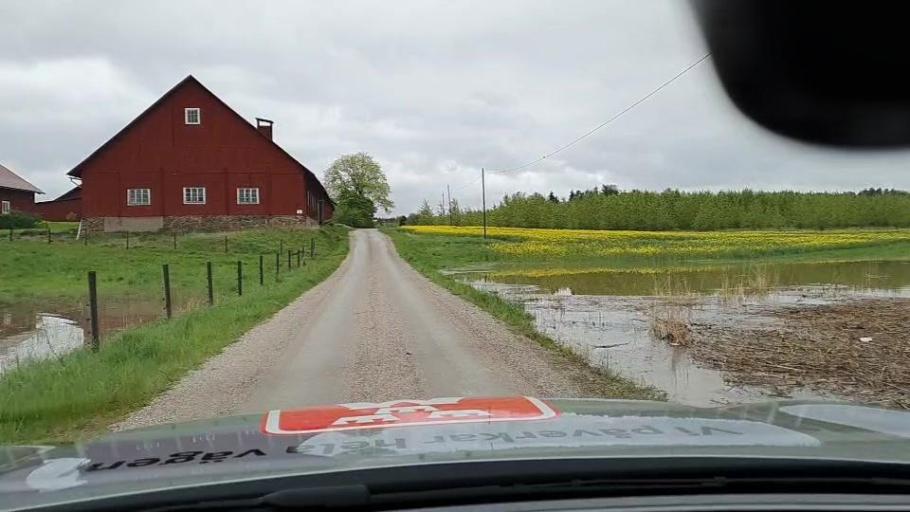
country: SE
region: Soedermanland
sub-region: Nykopings Kommun
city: Svalsta
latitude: 58.6407
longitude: 16.9333
